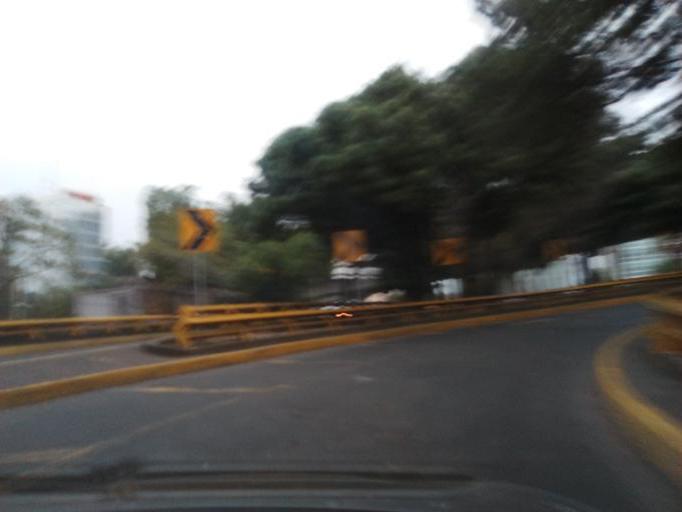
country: MX
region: Mexico City
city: Magdalena Contreras
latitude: 19.3121
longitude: -99.2189
